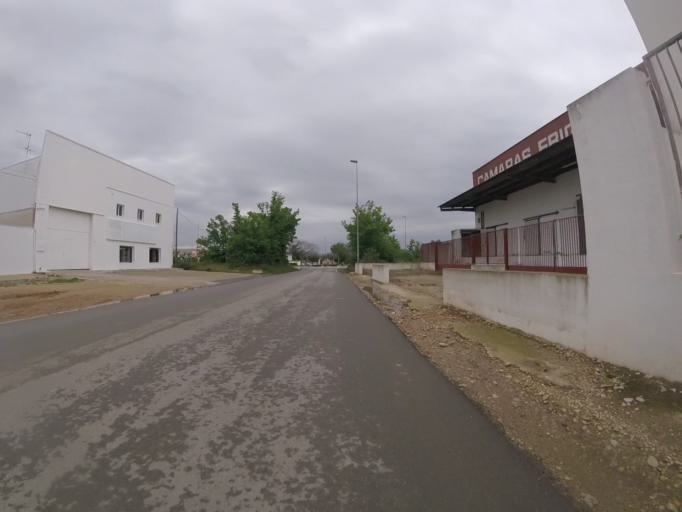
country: ES
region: Valencia
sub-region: Provincia de Castello
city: Alcala de Xivert
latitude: 40.3092
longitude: 0.2293
